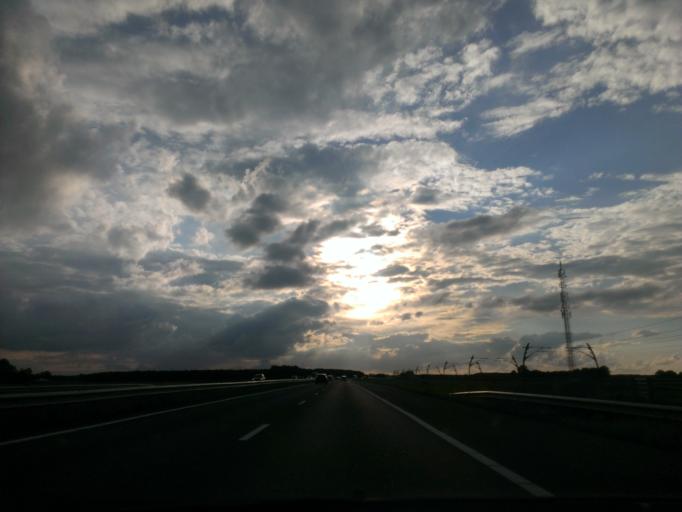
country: NL
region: South Holland
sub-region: Gemeente Leerdam
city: Leerdam
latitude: 51.8477
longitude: 5.1502
